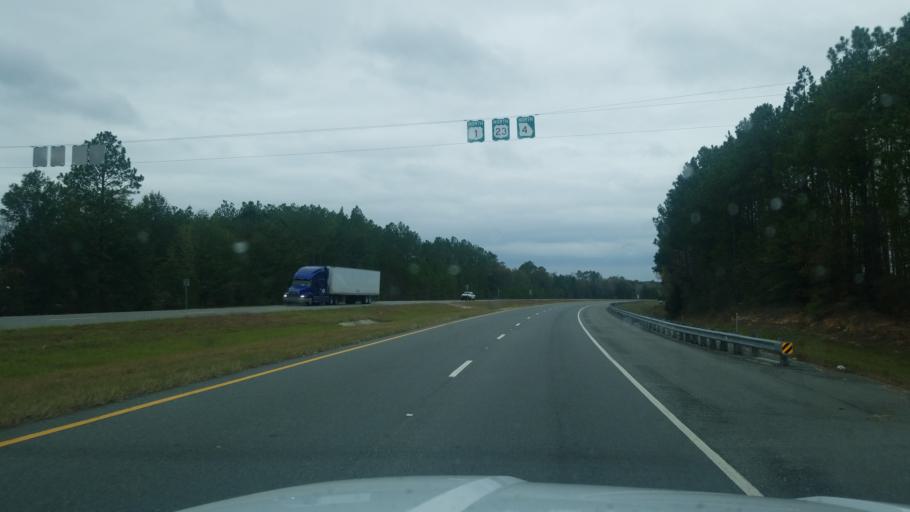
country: US
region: Georgia
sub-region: Ware County
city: Deenwood
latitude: 31.2919
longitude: -82.4491
